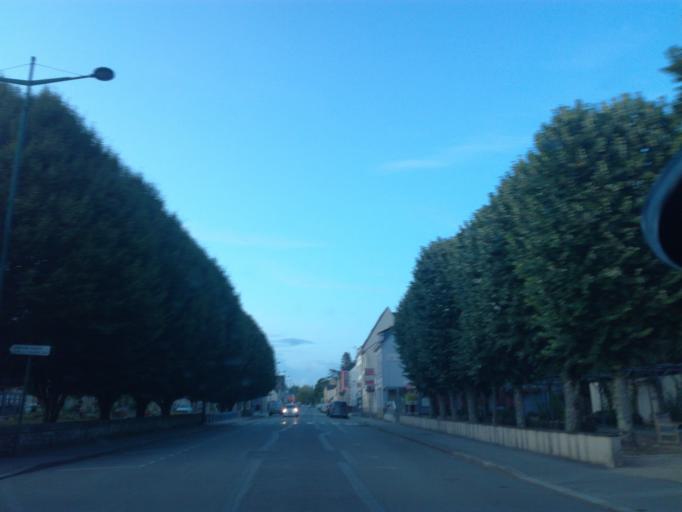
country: FR
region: Brittany
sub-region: Departement du Morbihan
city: Pontivy
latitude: 48.0710
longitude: -2.9641
